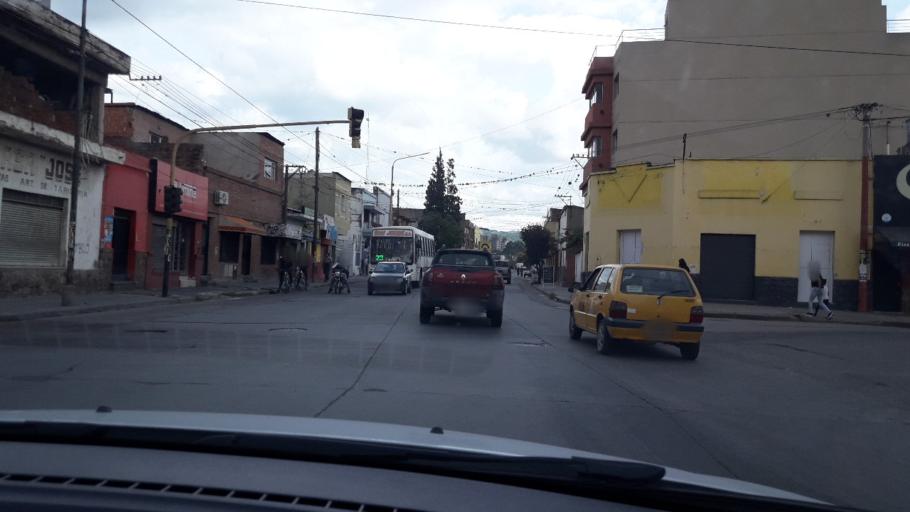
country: AR
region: Jujuy
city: San Salvador de Jujuy
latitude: -24.1948
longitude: -65.2893
